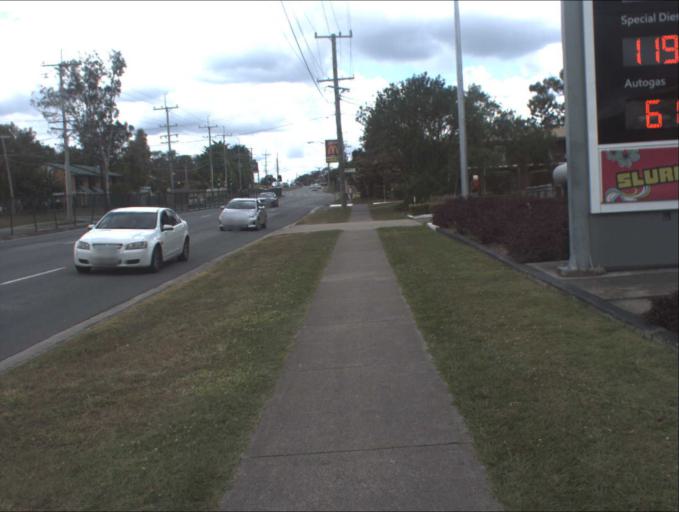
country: AU
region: Queensland
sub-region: Logan
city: Logan City
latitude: -27.6448
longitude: 153.1183
